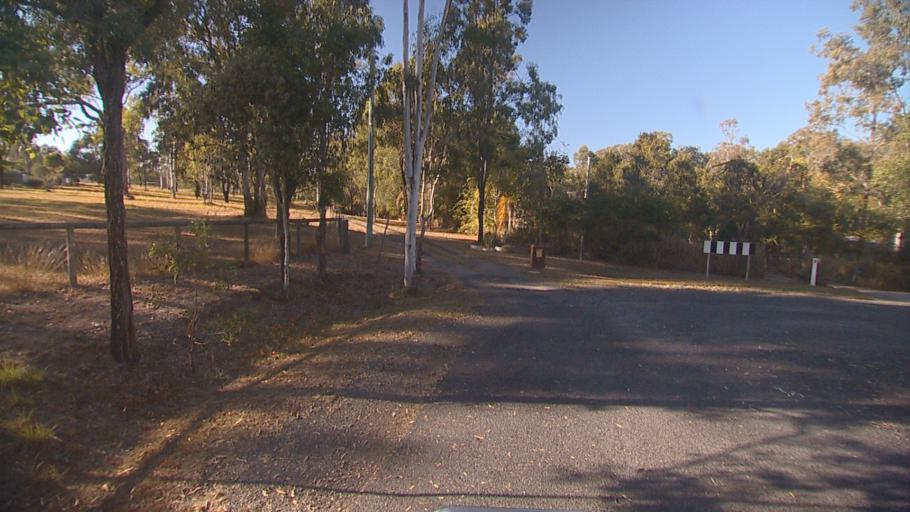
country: AU
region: Queensland
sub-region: Logan
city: North Maclean
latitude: -27.7984
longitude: 152.9900
